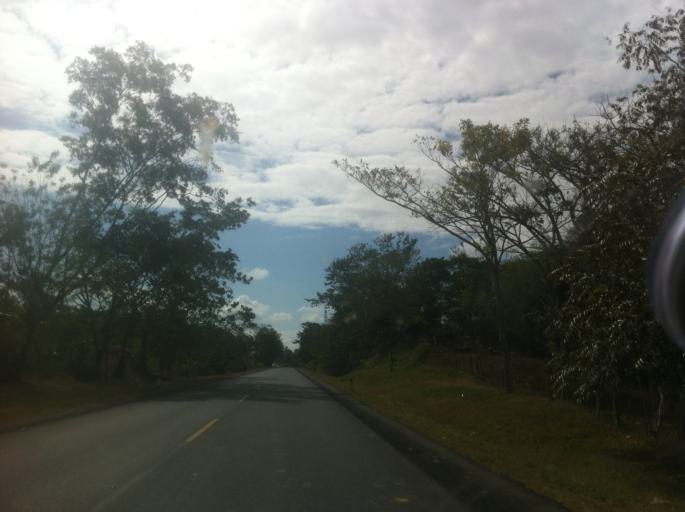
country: NI
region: Rio San Juan
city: San Carlos
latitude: 11.2903
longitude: -84.7240
